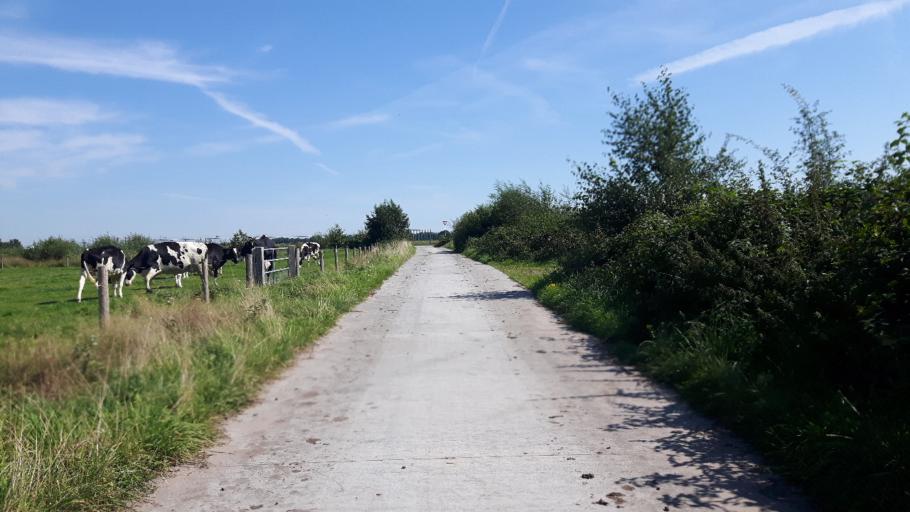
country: NL
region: Drenthe
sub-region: Gemeente Tynaarlo
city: Vries
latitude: 53.1099
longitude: 6.5540
